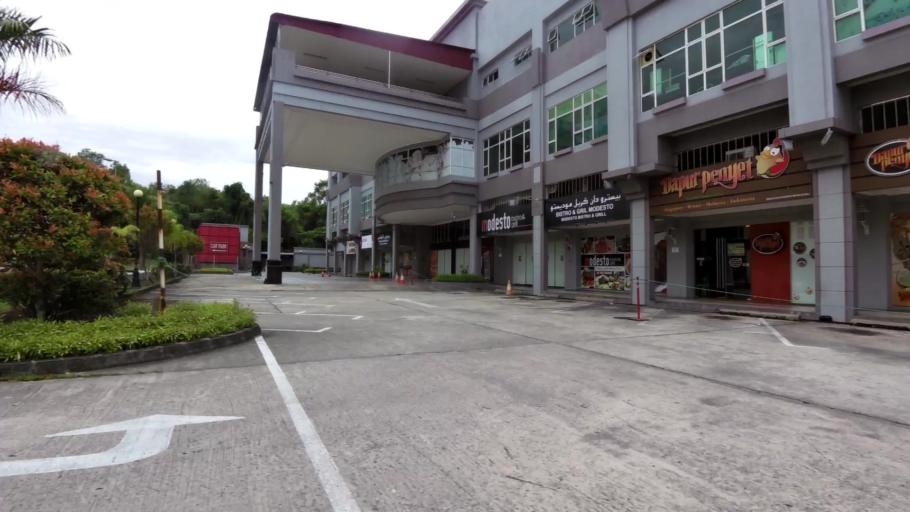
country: BN
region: Brunei and Muara
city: Bandar Seri Begawan
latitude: 4.9038
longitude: 114.9268
